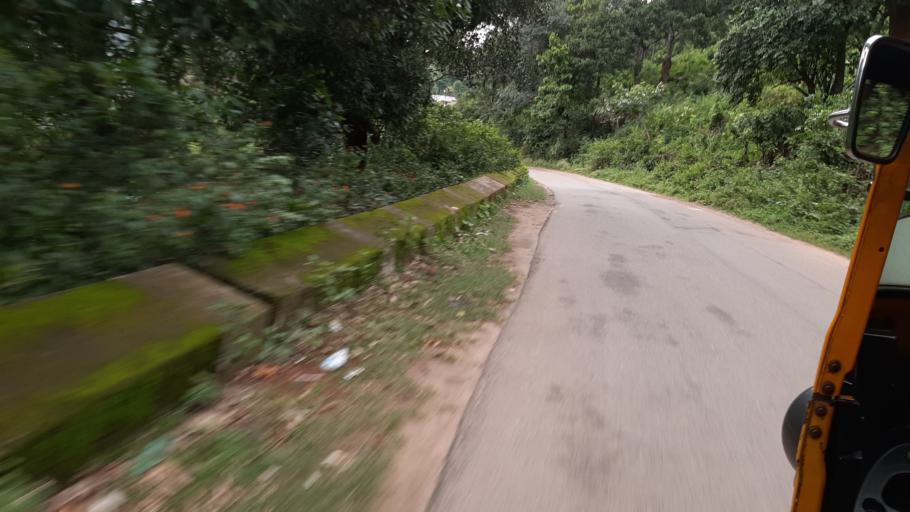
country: IN
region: Andhra Pradesh
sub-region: Vizianagaram District
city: Salur
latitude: 18.2368
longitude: 83.0032
